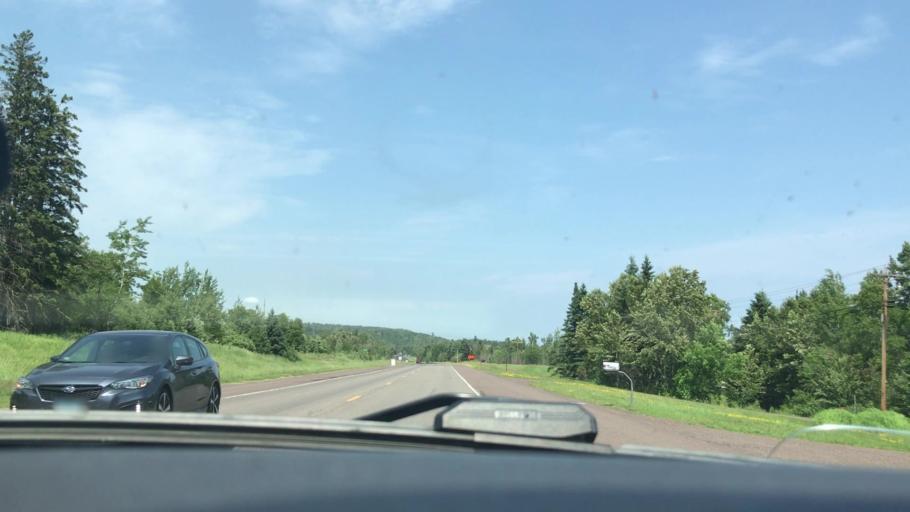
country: US
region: Minnesota
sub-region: Lake County
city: Silver Bay
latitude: 47.3249
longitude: -91.2136
